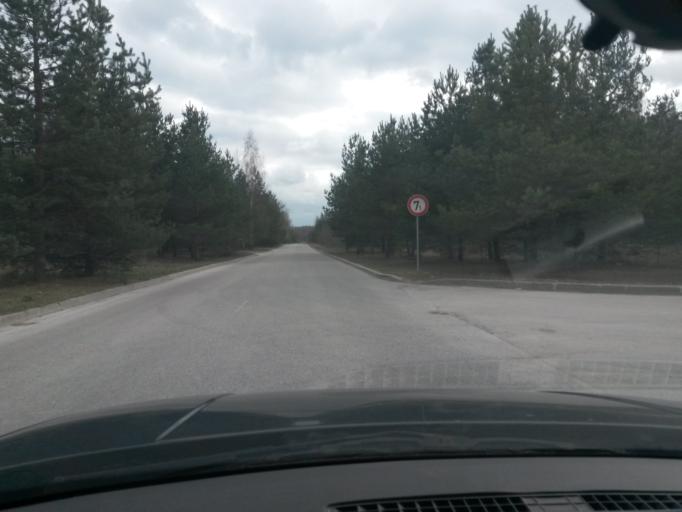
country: LV
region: Stopini
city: Ulbroka
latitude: 56.9009
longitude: 24.2470
